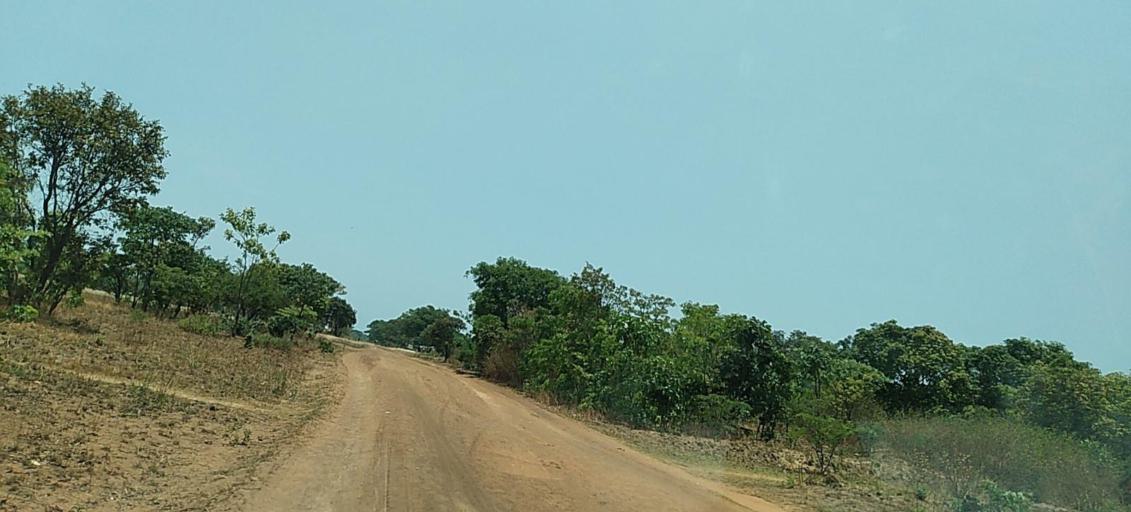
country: ZM
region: Copperbelt
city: Mpongwe
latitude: -13.7921
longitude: 27.8628
